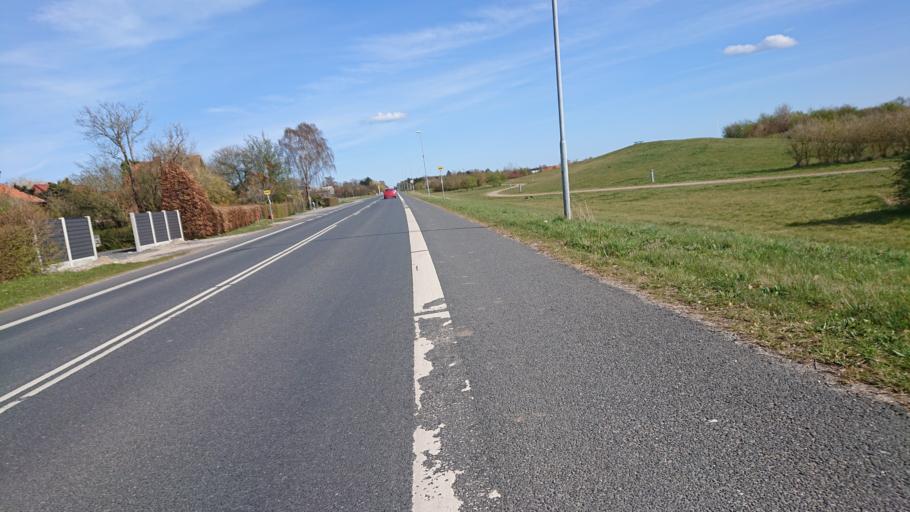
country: DK
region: South Denmark
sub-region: Nyborg Kommune
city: Nyborg
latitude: 55.3107
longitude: 10.7438
